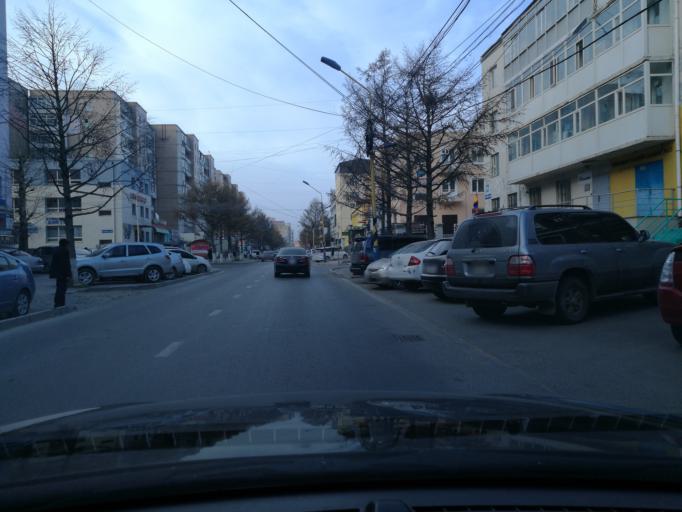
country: MN
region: Ulaanbaatar
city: Ulaanbaatar
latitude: 47.9259
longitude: 106.9273
